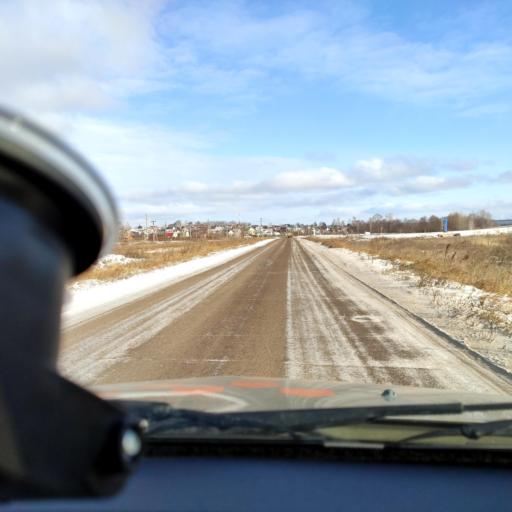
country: RU
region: Bashkortostan
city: Mikhaylovka
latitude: 54.7961
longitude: 55.7762
